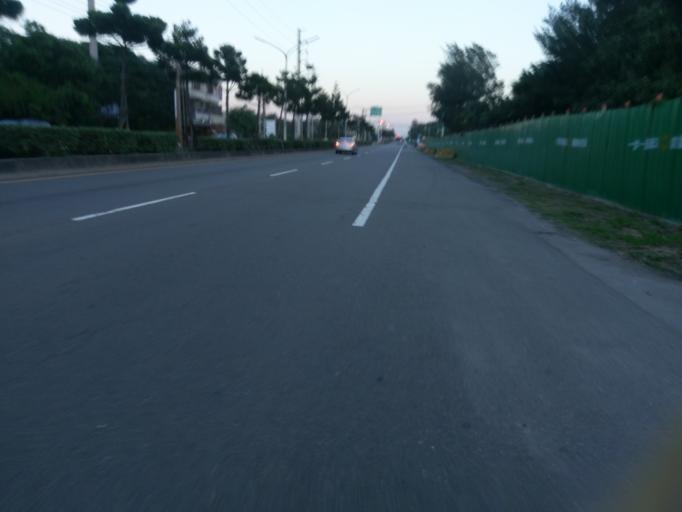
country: TW
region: Taiwan
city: Taoyuan City
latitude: 25.0550
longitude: 121.1366
